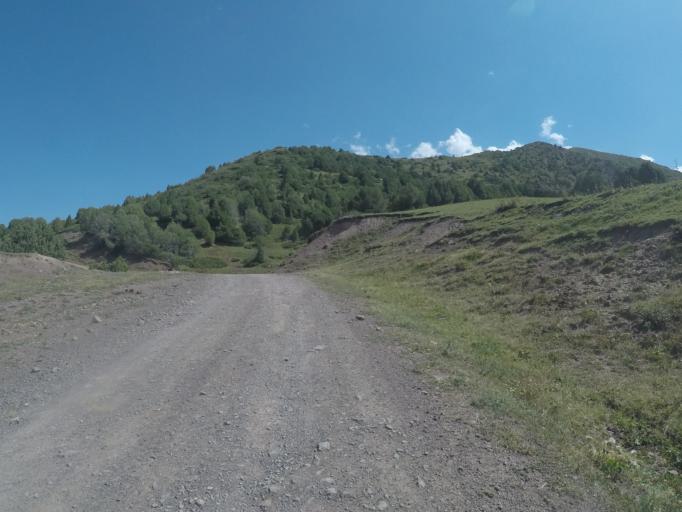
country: KG
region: Chuy
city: Bishkek
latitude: 42.6465
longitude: 74.5586
